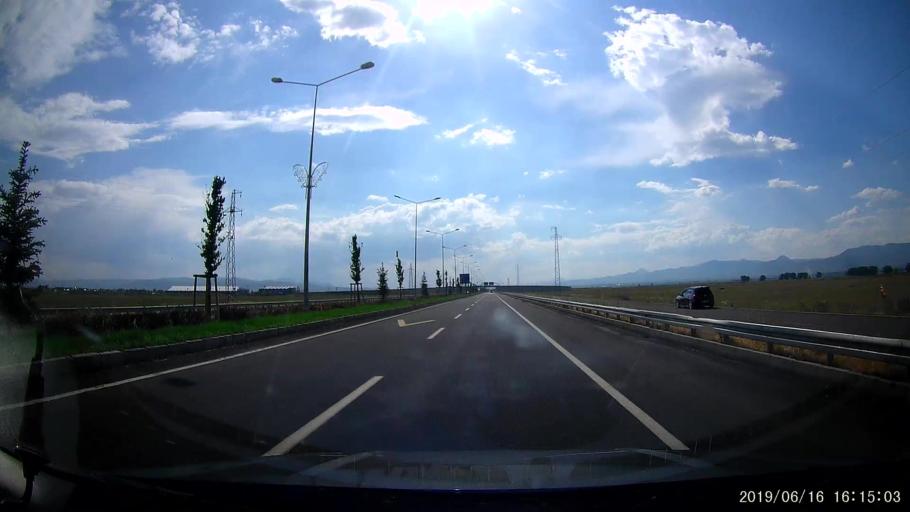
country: TR
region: Erzurum
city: Erzurum
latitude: 39.9615
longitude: 41.2344
